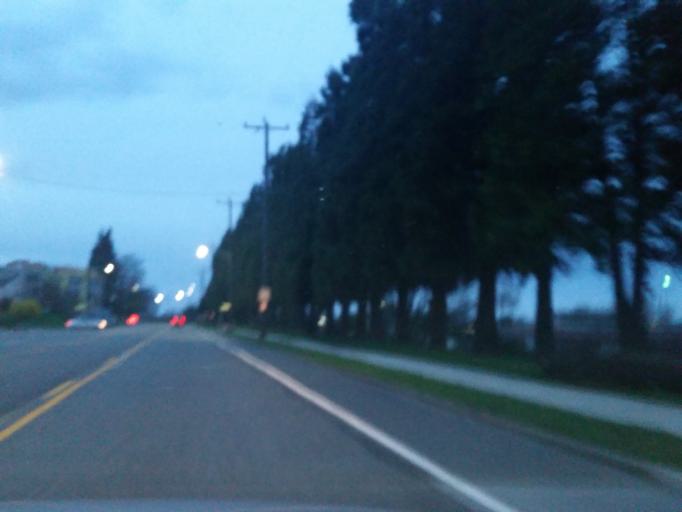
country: US
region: Washington
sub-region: King County
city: Seattle
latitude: 47.6533
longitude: -122.3840
